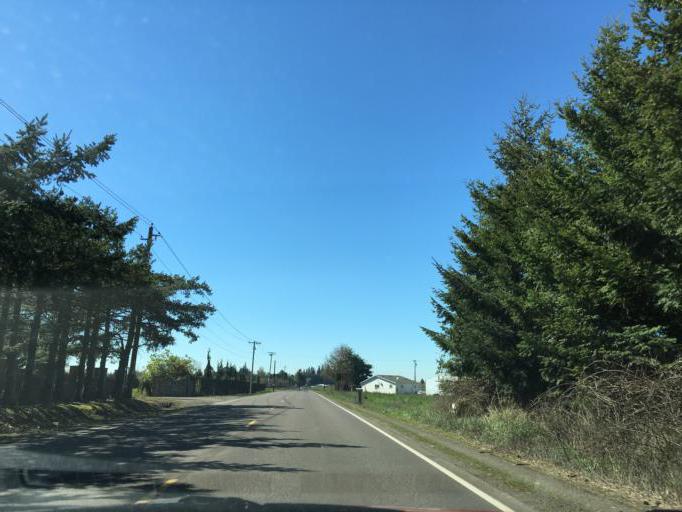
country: US
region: Oregon
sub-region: Marion County
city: Hubbard
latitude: 45.1443
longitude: -122.7549
